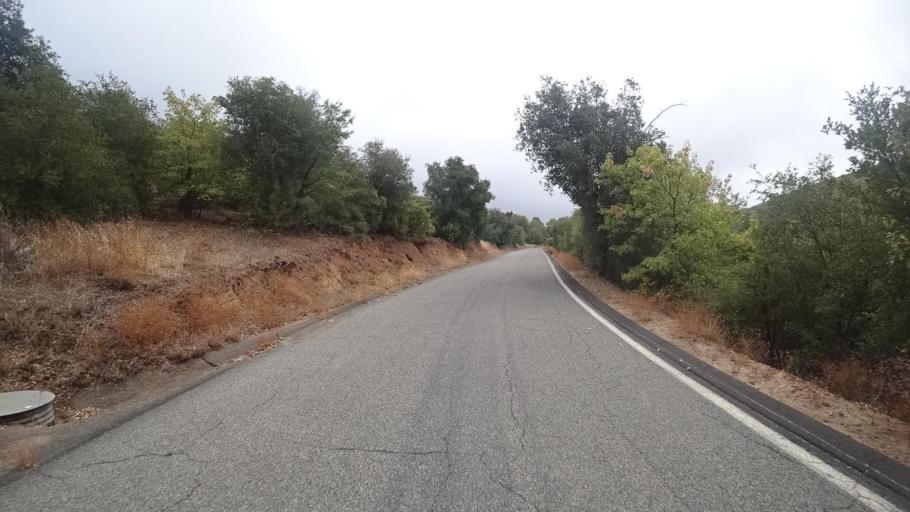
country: US
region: California
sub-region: San Diego County
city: Julian
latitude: 33.0075
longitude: -116.6215
